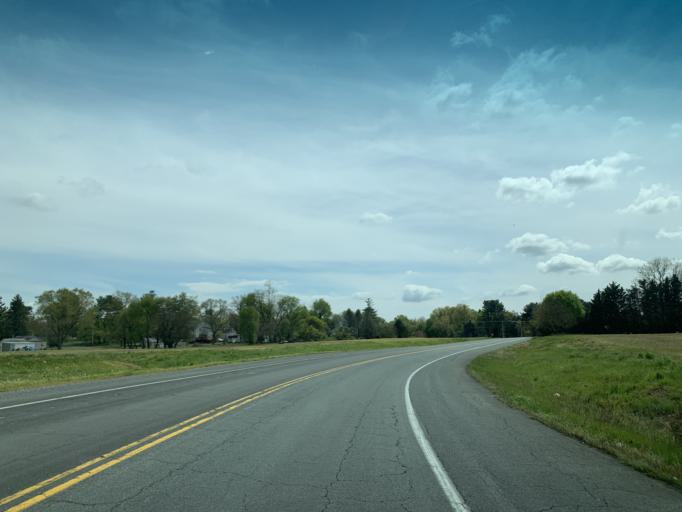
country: US
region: Maryland
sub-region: Harford County
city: Perryman
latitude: 39.4697
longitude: -76.2019
